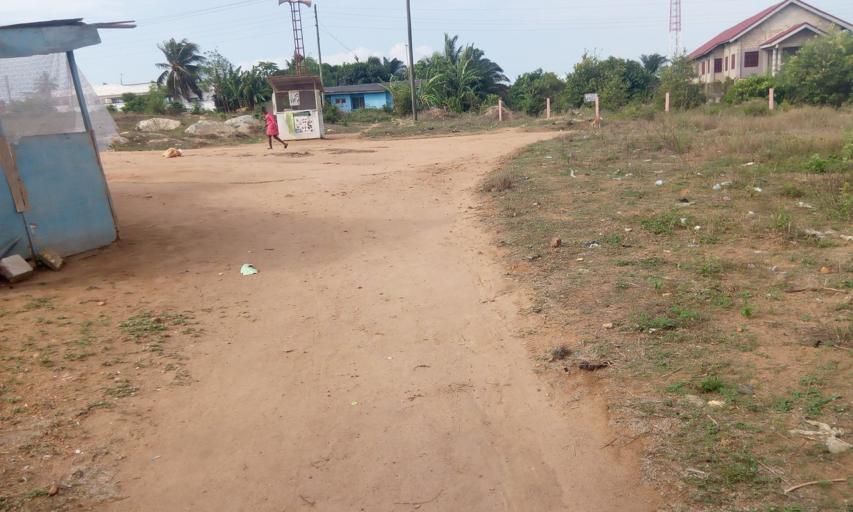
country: GH
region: Central
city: Winneba
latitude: 5.3587
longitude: -0.6227
